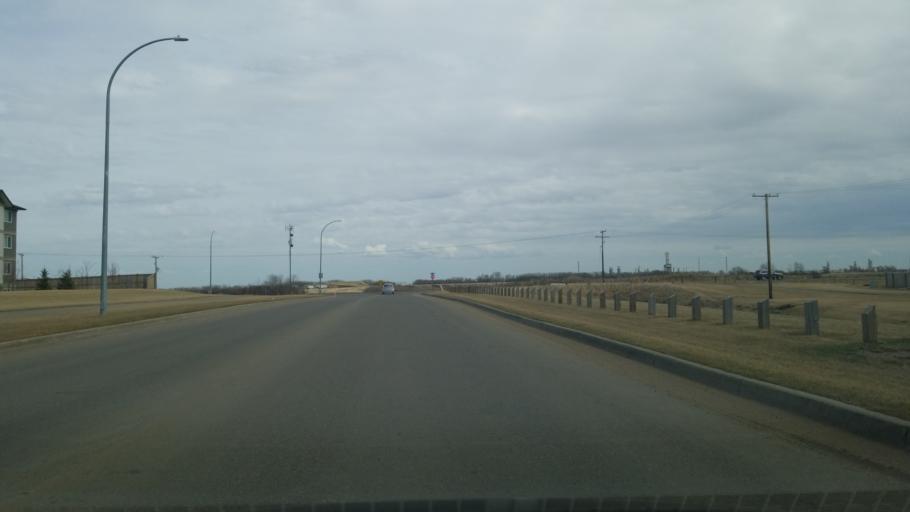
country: CA
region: Saskatchewan
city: Lloydminster
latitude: 53.2706
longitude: -109.9809
